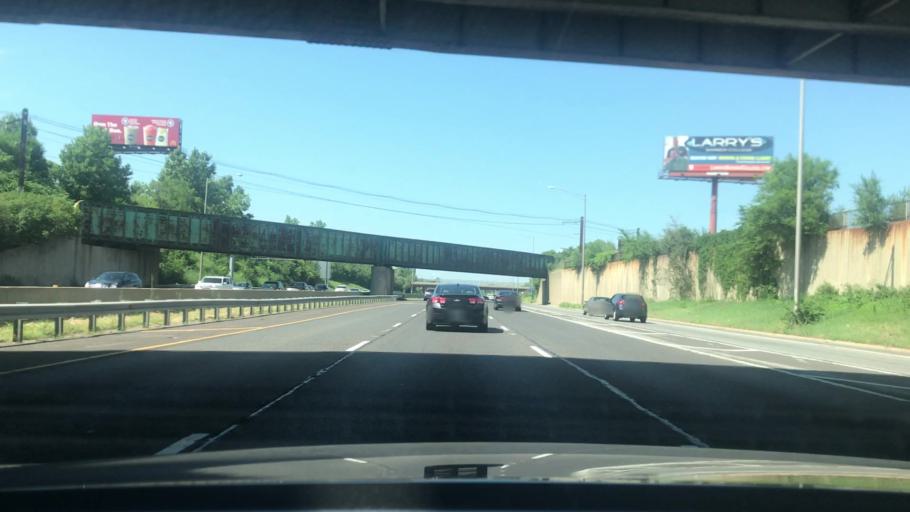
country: US
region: Illinois
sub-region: Cook County
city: Calumet Park
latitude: 41.6666
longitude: -87.6626
